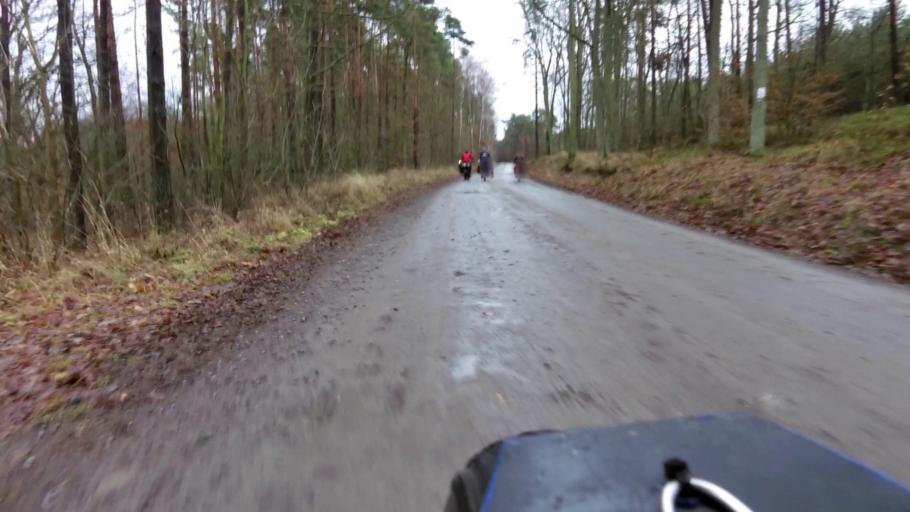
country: PL
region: Lubusz
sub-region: Powiat gorzowski
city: Witnica
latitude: 52.6918
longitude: 14.8571
